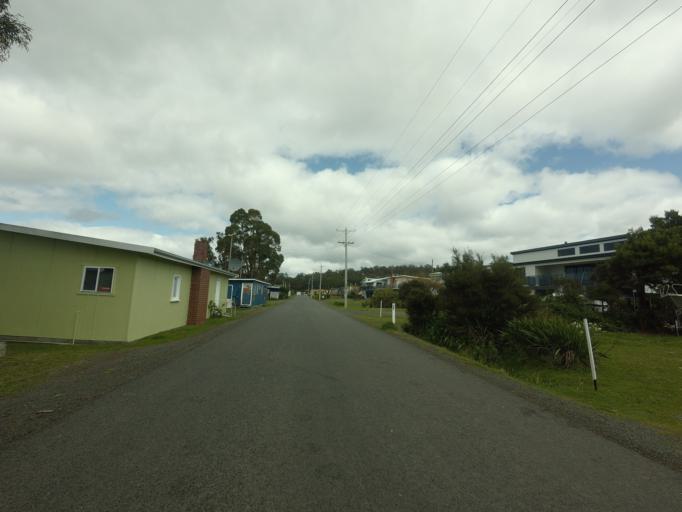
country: AU
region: Tasmania
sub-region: Huon Valley
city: Geeveston
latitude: -43.4379
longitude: 146.9621
